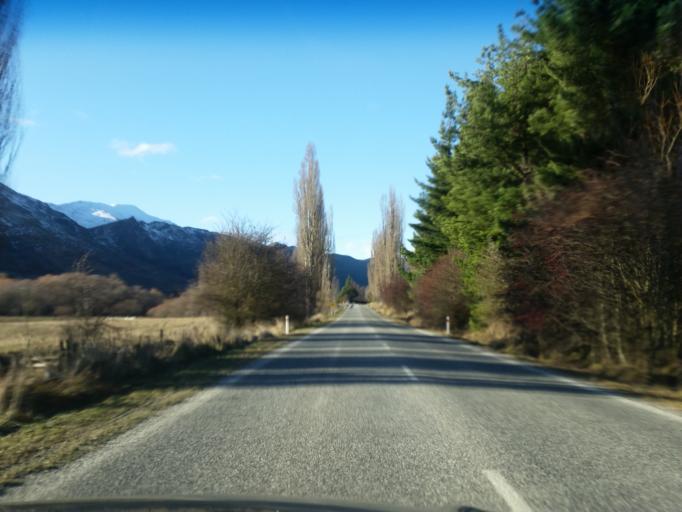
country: NZ
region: Otago
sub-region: Queenstown-Lakes District
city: Arrowtown
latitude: -44.9578
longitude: 168.7311
